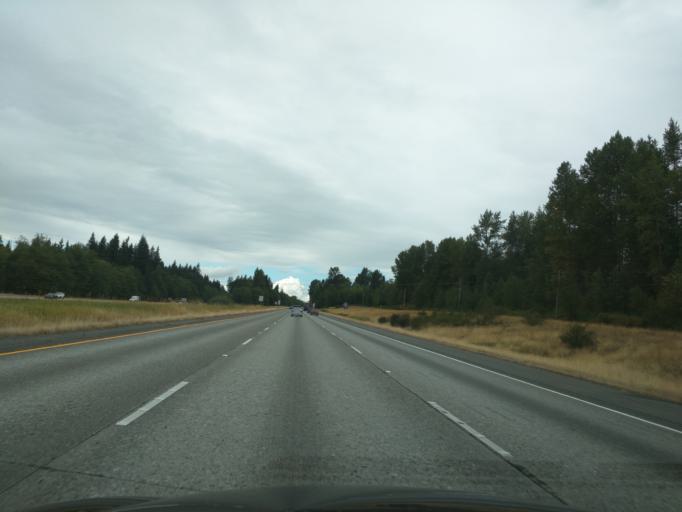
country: US
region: Washington
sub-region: Snohomish County
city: Bryant
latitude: 48.2437
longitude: -122.2454
